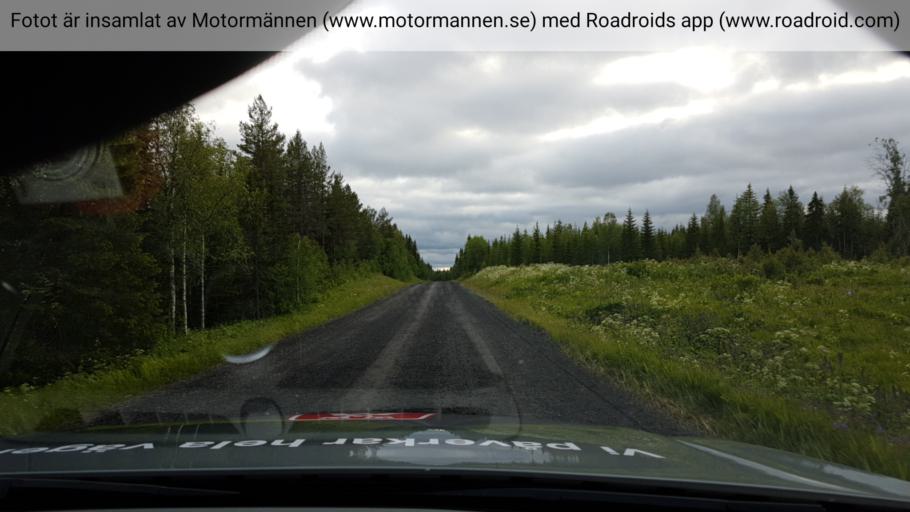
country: SE
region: Jaemtland
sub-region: OEstersunds Kommun
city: Lit
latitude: 63.6356
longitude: 15.0570
